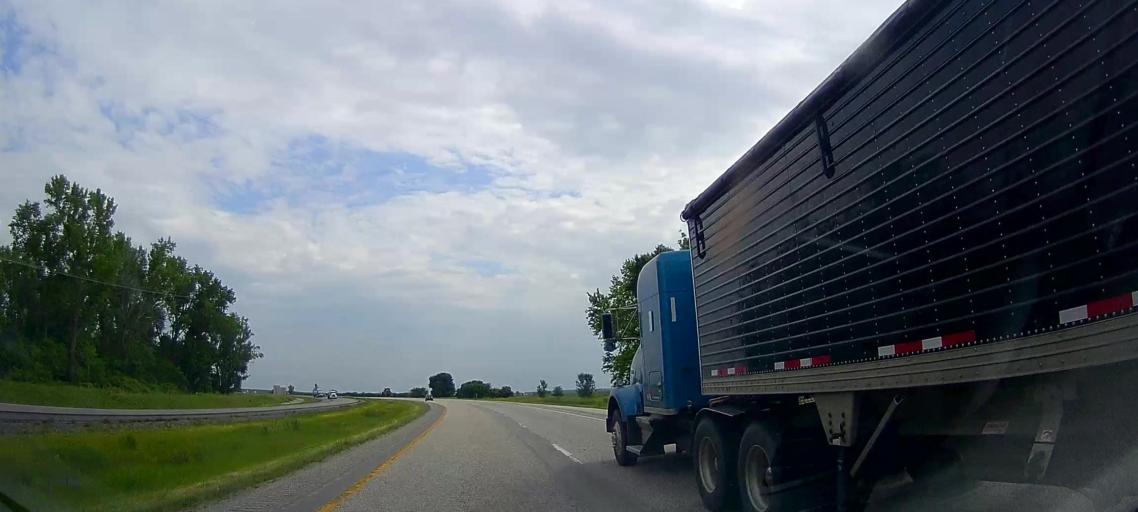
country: US
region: Nebraska
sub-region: Burt County
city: Tekamah
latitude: 41.7870
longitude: -96.0529
